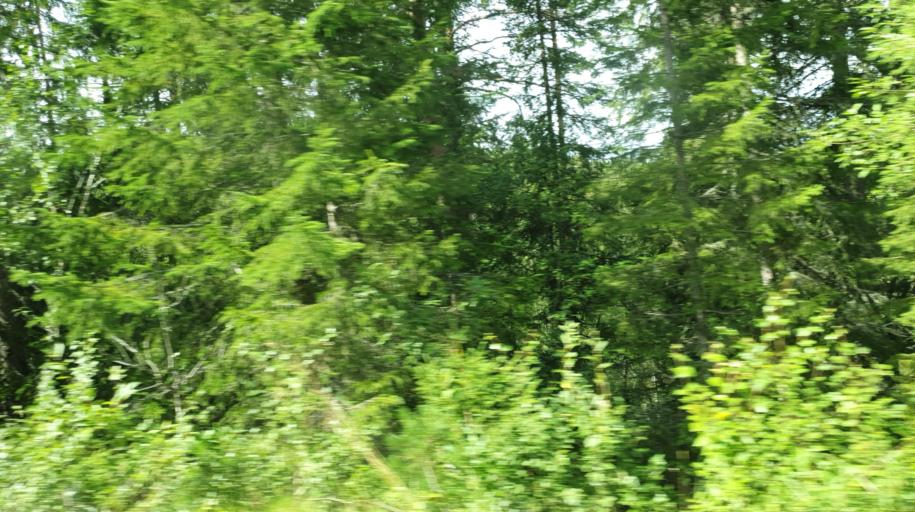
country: NO
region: Nord-Trondelag
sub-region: Levanger
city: Skogn
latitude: 63.5920
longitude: 11.2579
